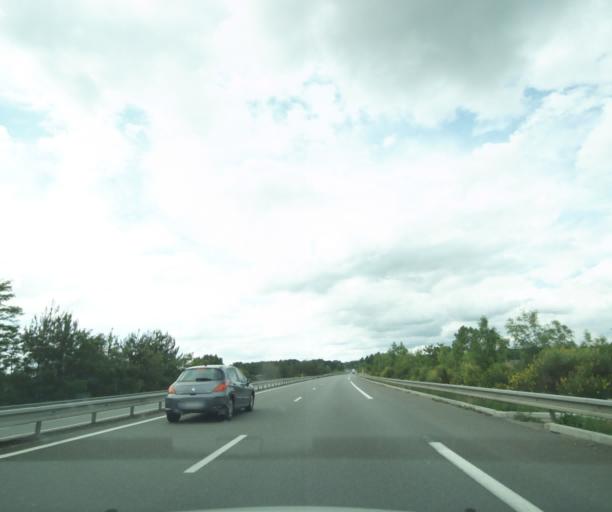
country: FR
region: Centre
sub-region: Departement du Cher
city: Vierzon
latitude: 47.2126
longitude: 2.1152
